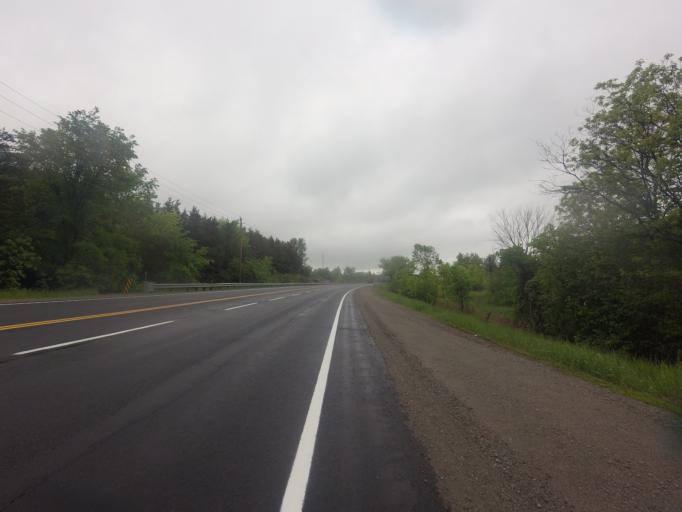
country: CA
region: Ontario
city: Perth
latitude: 44.7140
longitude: -76.1747
